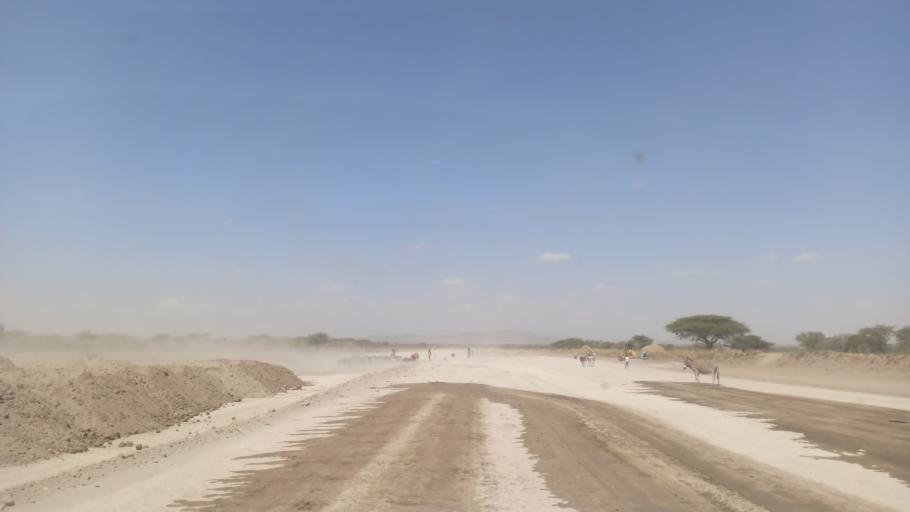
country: ET
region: Oromiya
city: Ziway
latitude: 7.7398
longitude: 38.6205
